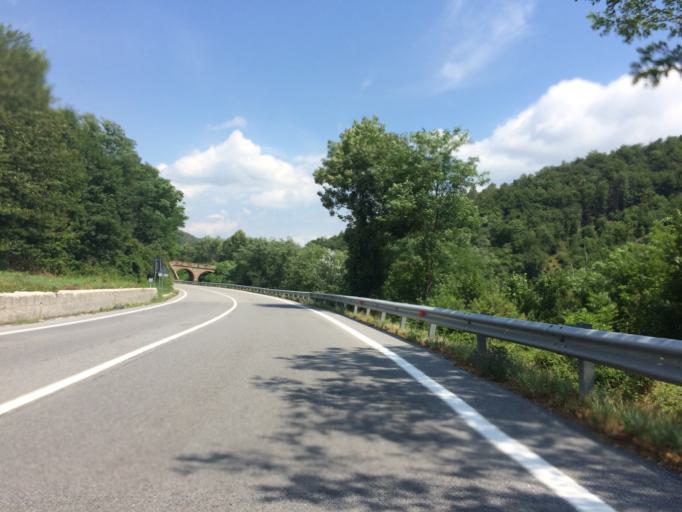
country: IT
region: Piedmont
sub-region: Provincia di Cuneo
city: Priola
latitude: 44.2293
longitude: 8.0174
